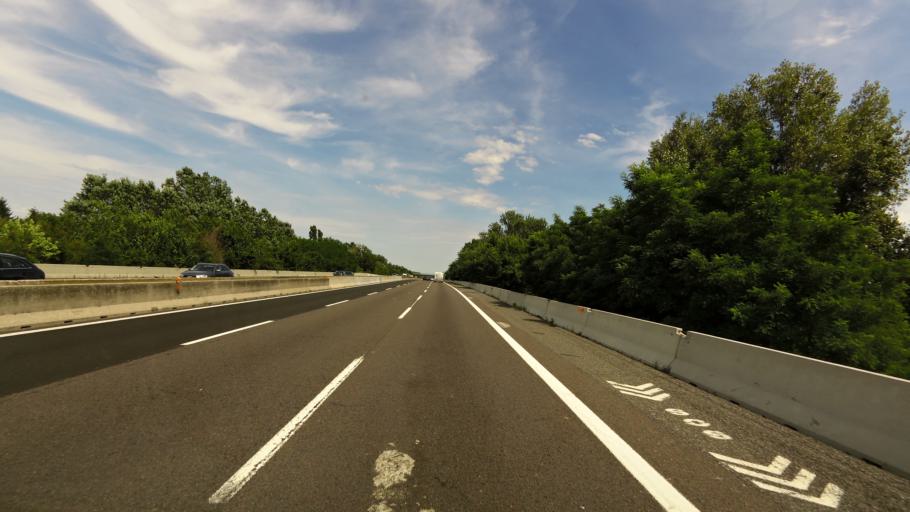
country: IT
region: Emilia-Romagna
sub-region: Provincia di Bologna
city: Osteria Grande
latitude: 44.4600
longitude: 11.5070
